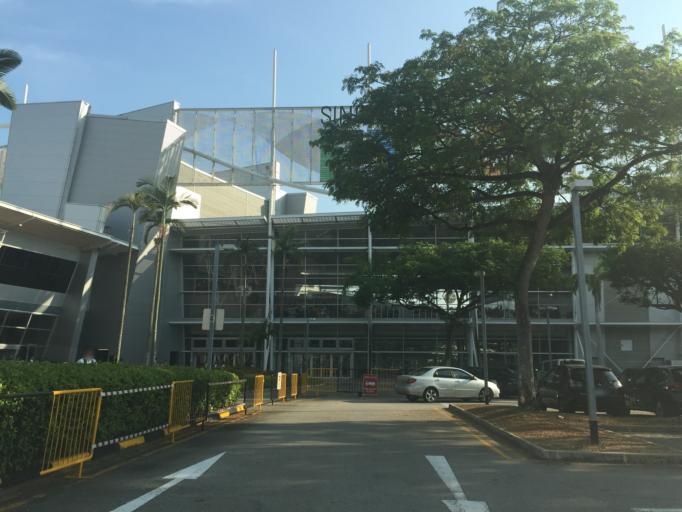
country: SG
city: Singapore
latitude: 1.3338
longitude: 103.9585
